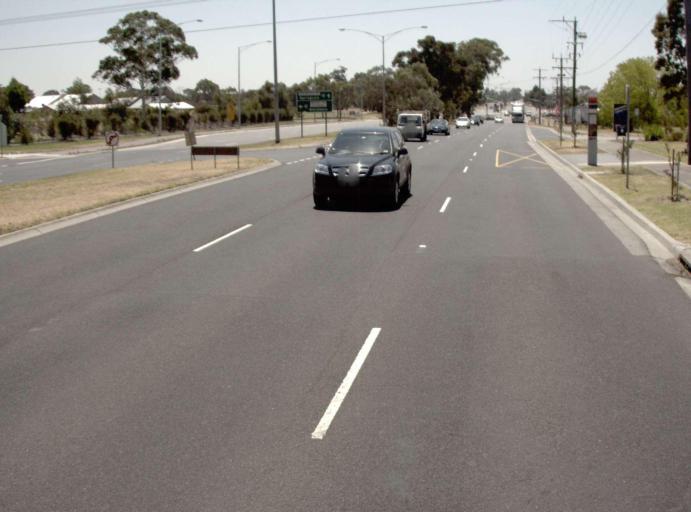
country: AU
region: Victoria
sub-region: Kingston
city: Dingley Village
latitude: -37.9867
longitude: 145.1455
